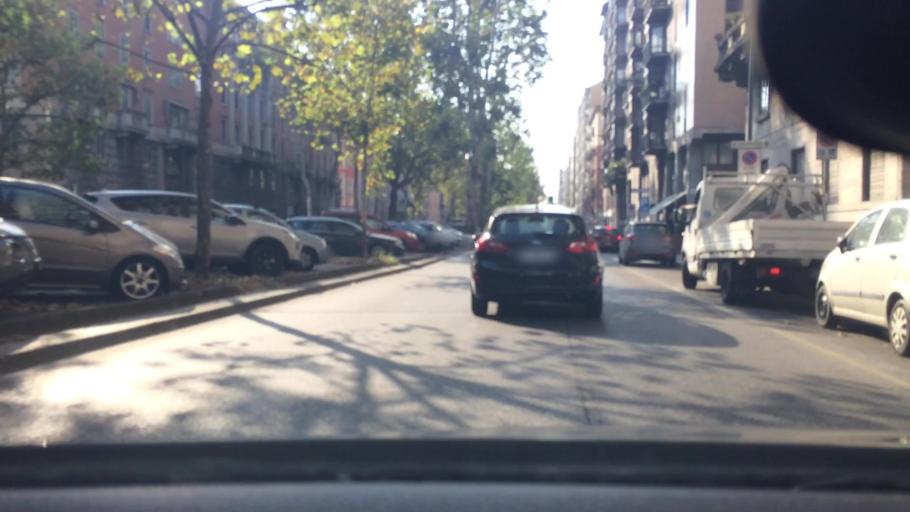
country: IT
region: Lombardy
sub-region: Citta metropolitana di Milano
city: Milano
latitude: 45.4885
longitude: 9.2109
